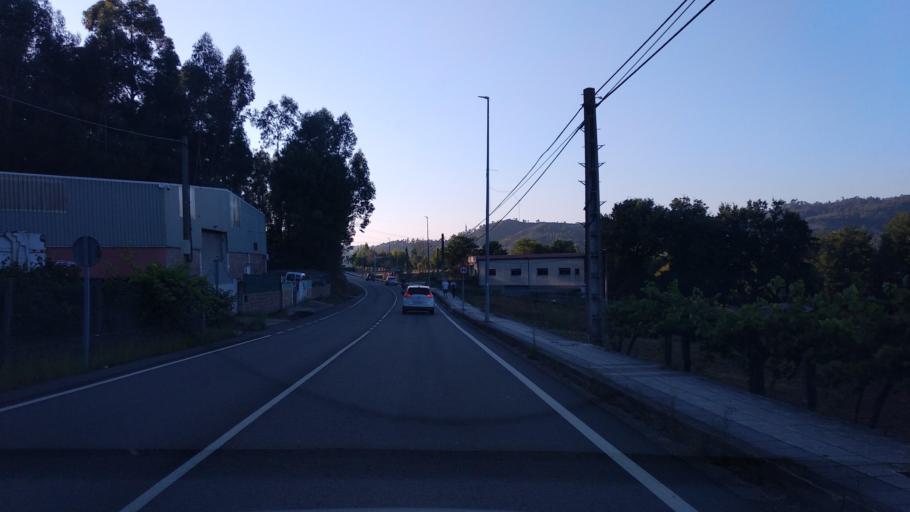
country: ES
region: Galicia
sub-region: Provincia de Pontevedra
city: Redondela
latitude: 42.3379
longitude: -8.5877
